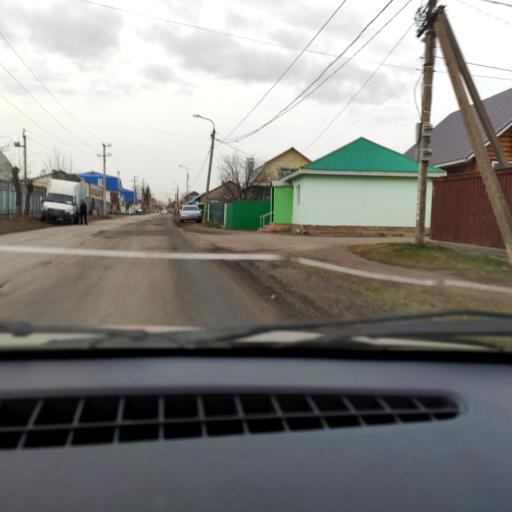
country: RU
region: Bashkortostan
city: Ufa
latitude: 54.7325
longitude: 55.8960
